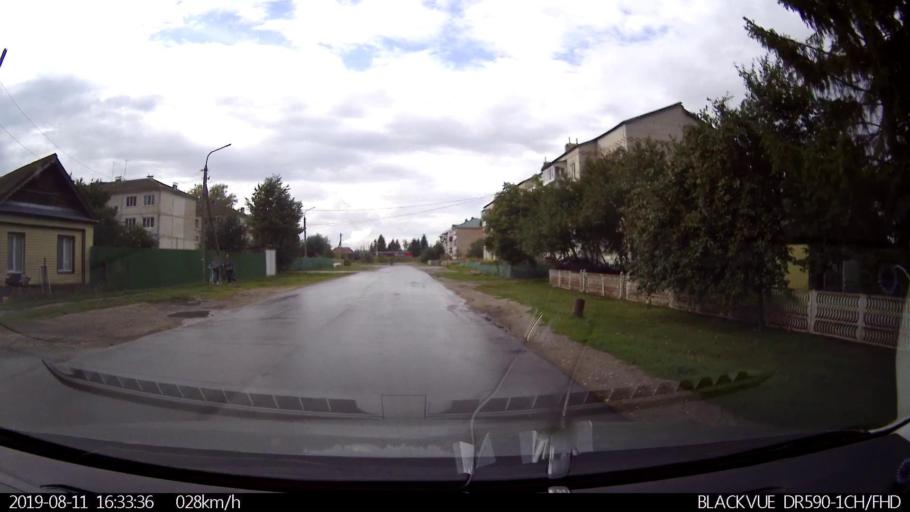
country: RU
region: Ulyanovsk
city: Mayna
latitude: 54.1153
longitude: 47.6249
